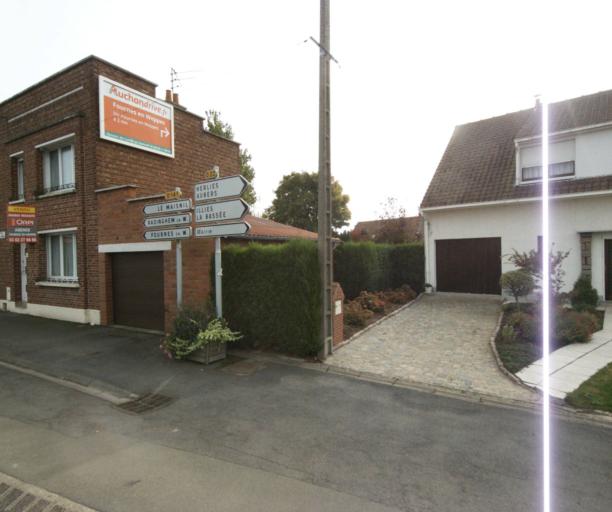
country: FR
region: Nord-Pas-de-Calais
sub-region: Departement du Nord
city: Herlies
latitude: 50.6061
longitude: 2.8546
